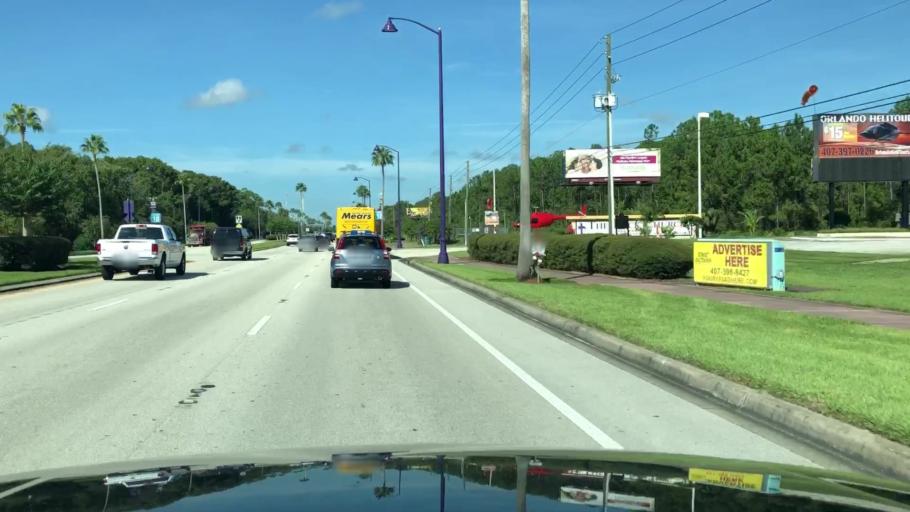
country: US
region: Florida
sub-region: Osceola County
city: Celebration
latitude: 28.3330
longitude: -81.5030
